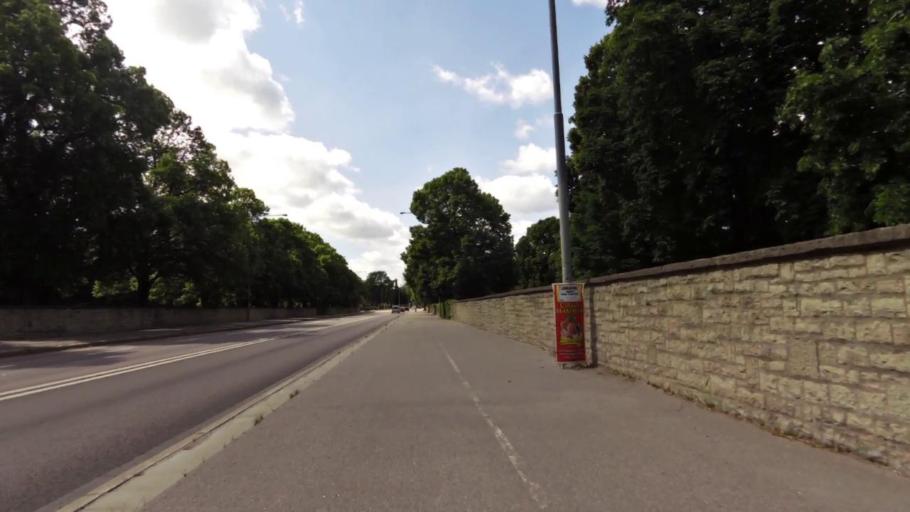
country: SE
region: OEstergoetland
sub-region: Linkopings Kommun
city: Linkoping
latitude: 58.4085
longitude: 15.6060
